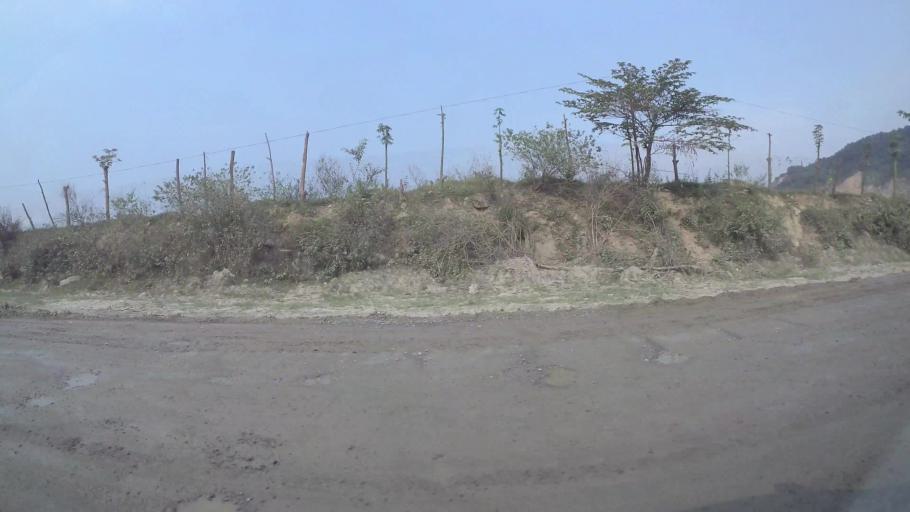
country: VN
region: Da Nang
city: Lien Chieu
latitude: 16.0398
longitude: 108.1518
